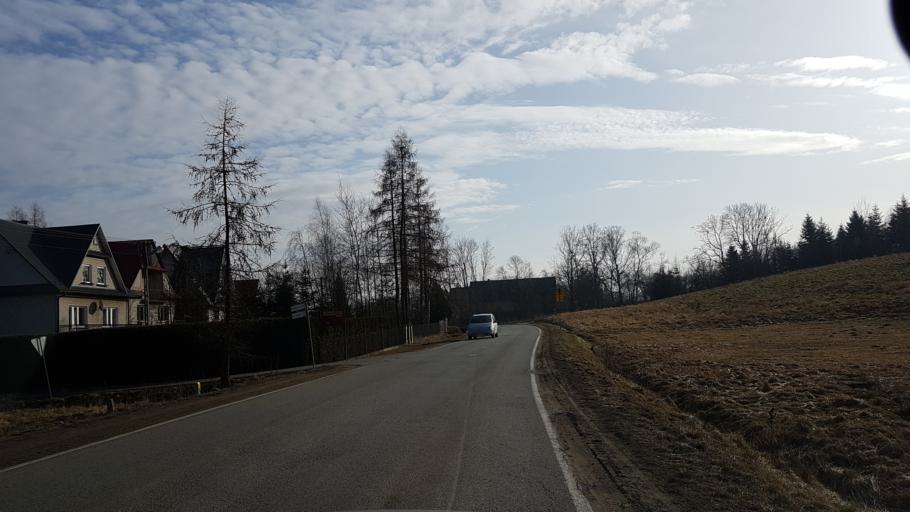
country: PL
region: Lesser Poland Voivodeship
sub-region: Powiat limanowski
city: Lukowica
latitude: 49.6506
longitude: 20.5006
